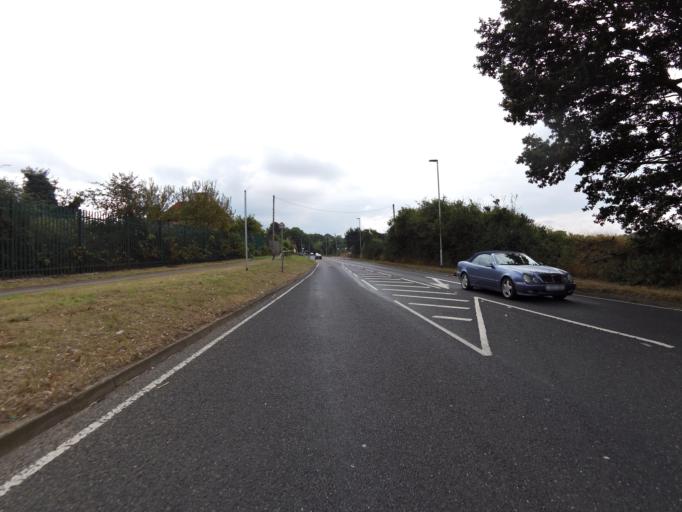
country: GB
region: England
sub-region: Hertfordshire
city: Shenley AV
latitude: 51.7048
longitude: -0.2910
